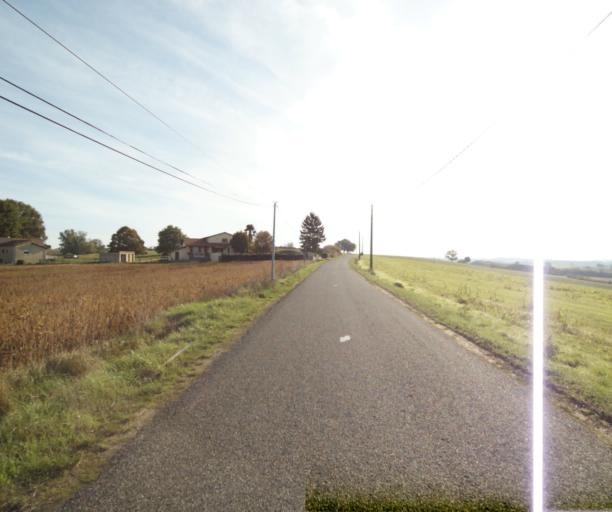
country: FR
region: Midi-Pyrenees
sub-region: Departement de la Haute-Garonne
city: Villemur-sur-Tarn
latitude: 43.9023
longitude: 1.4813
